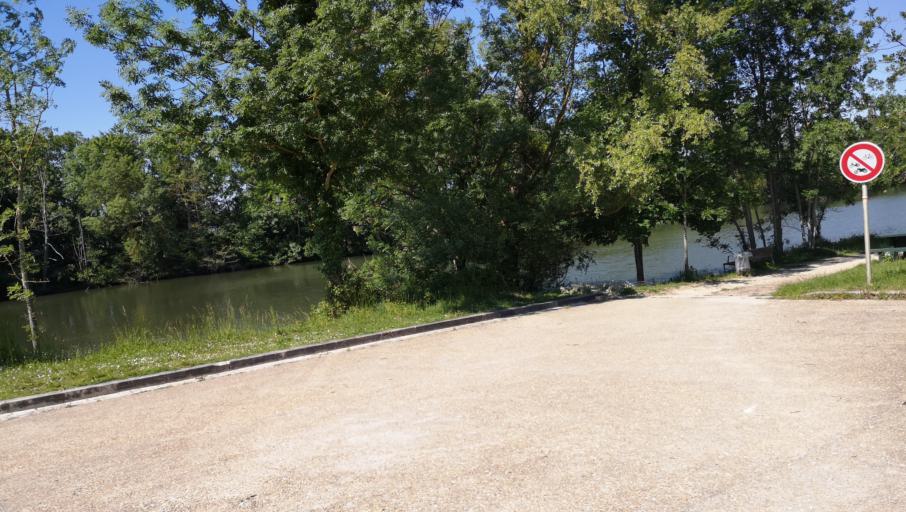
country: FR
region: Centre
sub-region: Departement du Loiret
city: Saint-Hilaire-Saint-Mesmin
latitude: 47.8669
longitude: 1.8270
